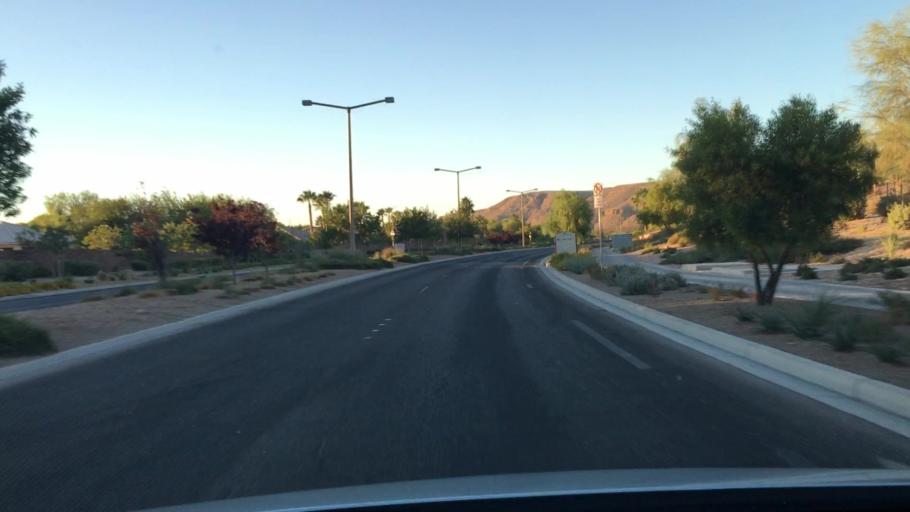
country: US
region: Nevada
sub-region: Clark County
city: Summerlin South
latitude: 36.1070
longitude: -115.3275
